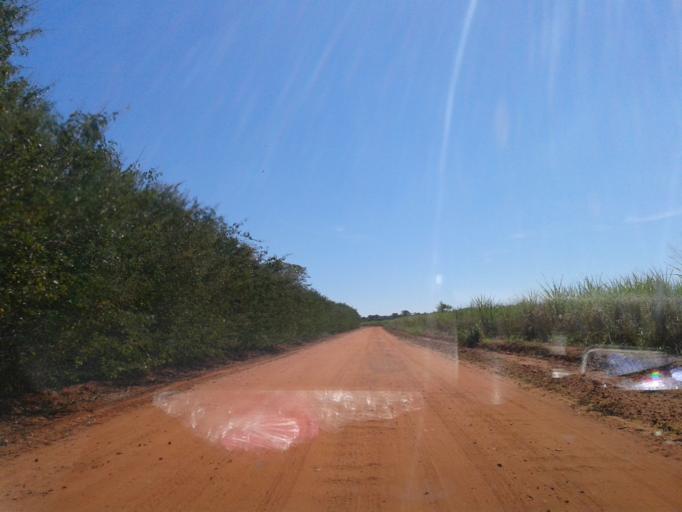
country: BR
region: Minas Gerais
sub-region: Santa Vitoria
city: Santa Vitoria
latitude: -19.0251
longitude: -50.3650
